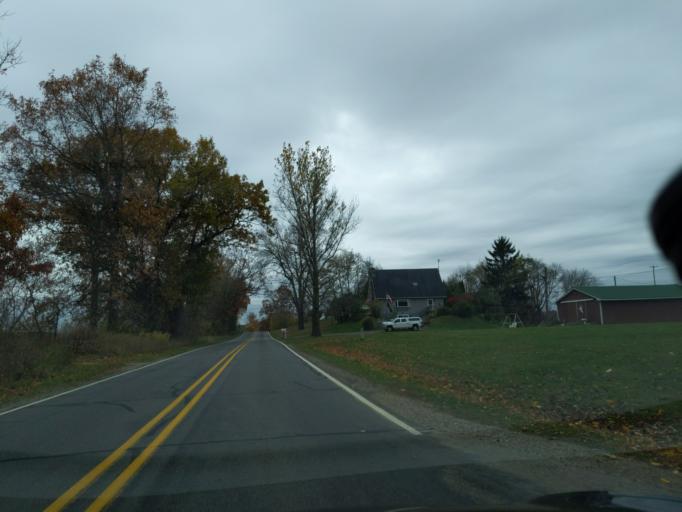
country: US
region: Michigan
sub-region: Eaton County
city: Eaton Rapids
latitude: 42.3714
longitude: -84.6005
